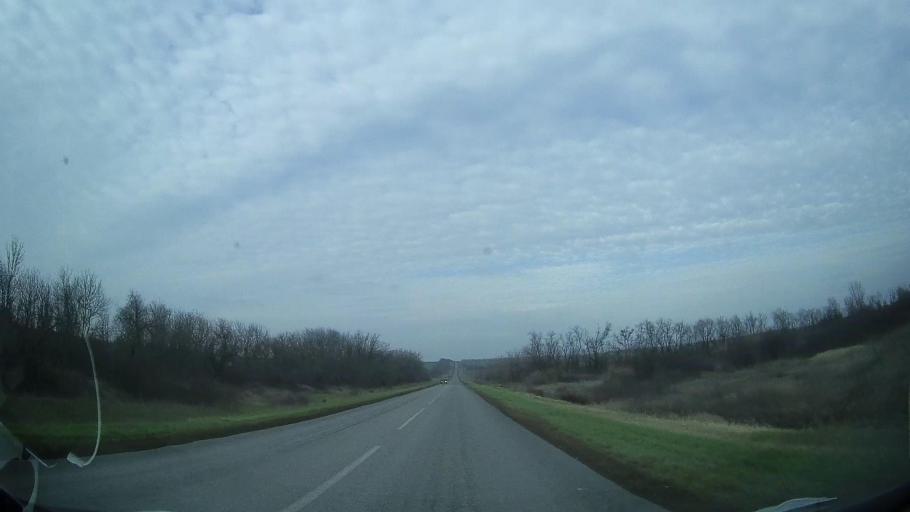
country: RU
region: Rostov
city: Zernograd
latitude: 46.8918
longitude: 40.3389
